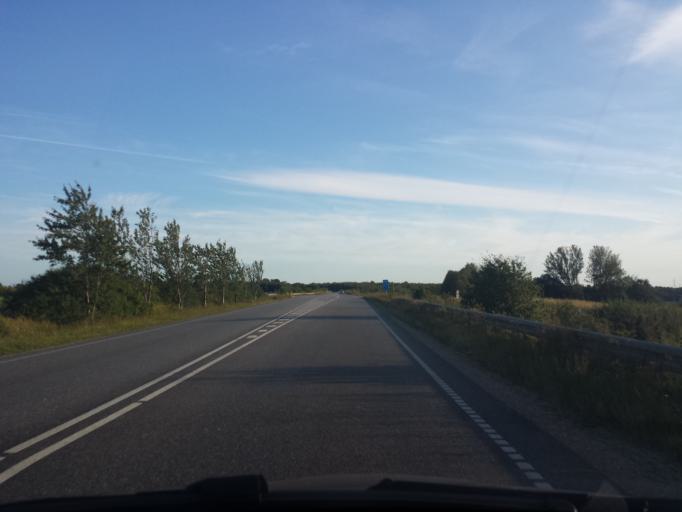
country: DK
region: Capital Region
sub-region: Frederikssund Kommune
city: Frederikssund
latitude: 55.8149
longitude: 12.1038
